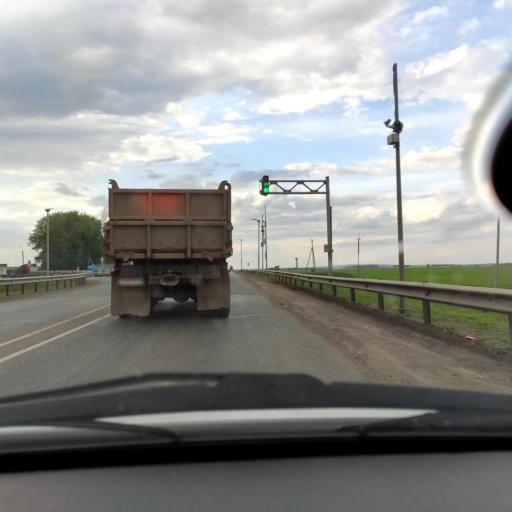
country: RU
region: Bashkortostan
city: Dyurtyuli
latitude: 55.4270
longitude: 54.8067
